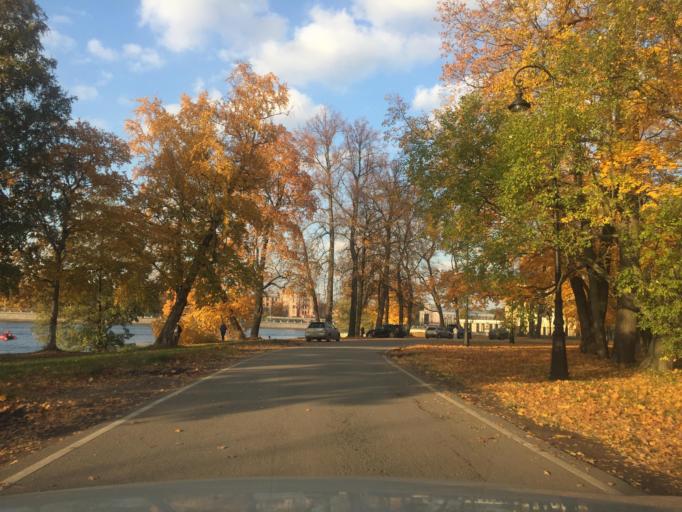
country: RU
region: St.-Petersburg
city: Novaya Derevnya
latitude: 59.9790
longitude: 30.2751
